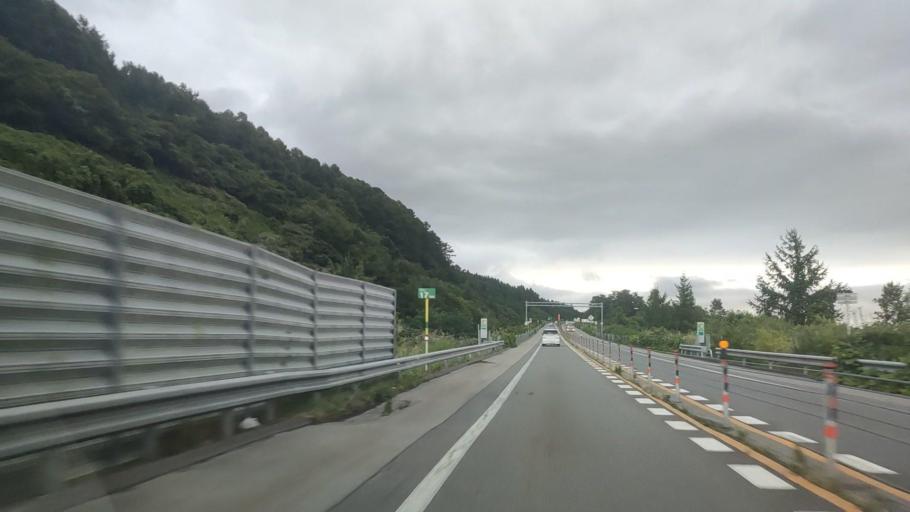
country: JP
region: Hokkaido
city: Nanae
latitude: 41.9121
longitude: 140.6922
